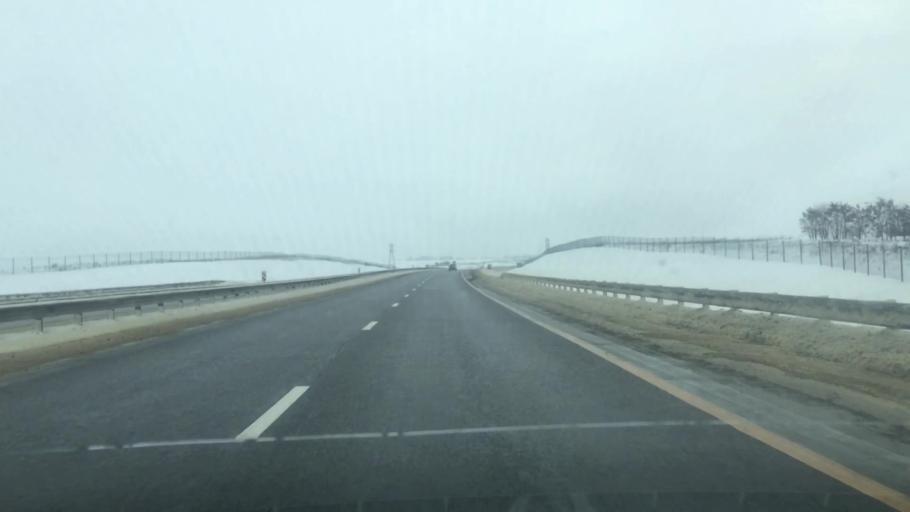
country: RU
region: Tula
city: Yefremov
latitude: 53.1479
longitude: 38.2493
